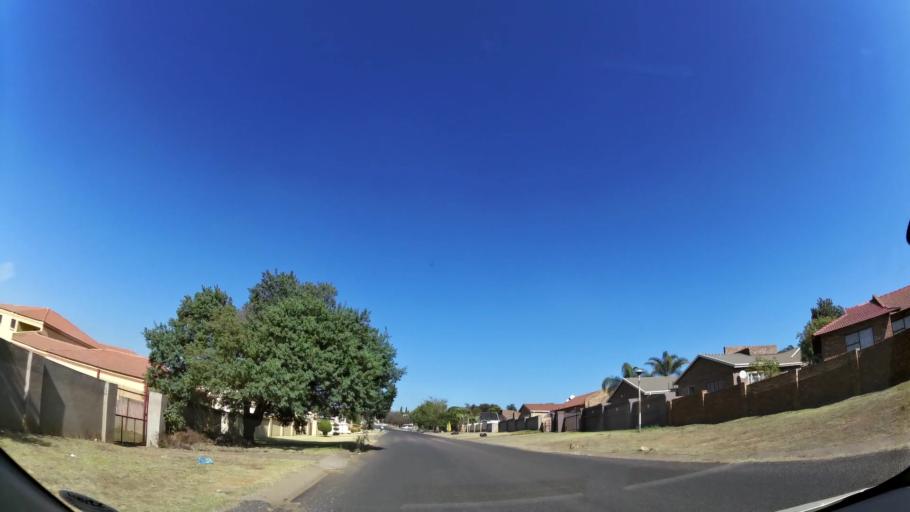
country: ZA
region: Mpumalanga
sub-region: Nkangala District Municipality
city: Witbank
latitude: -25.8611
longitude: 29.2425
